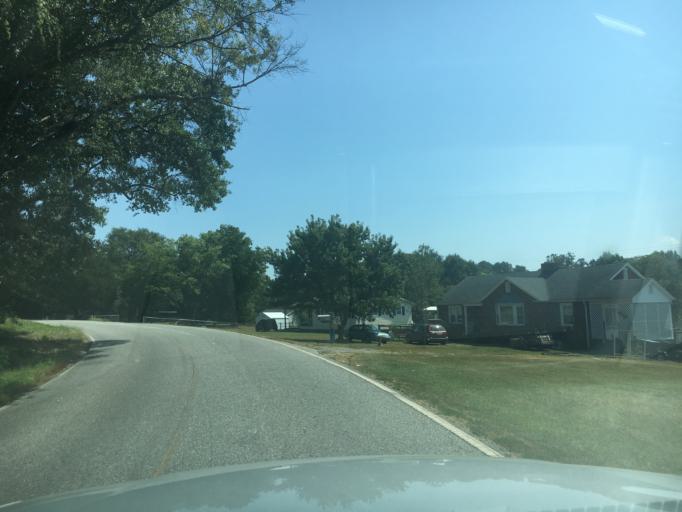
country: US
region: South Carolina
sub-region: Spartanburg County
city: Inman
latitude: 35.1205
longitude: -82.0373
